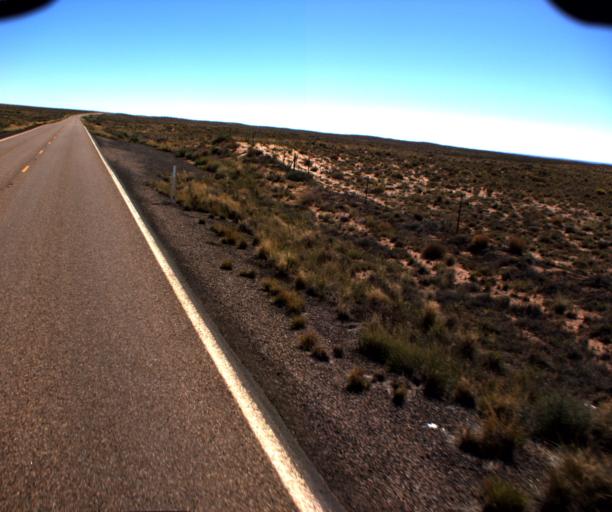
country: US
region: Arizona
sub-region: Navajo County
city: Holbrook
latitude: 35.0427
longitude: -110.0927
